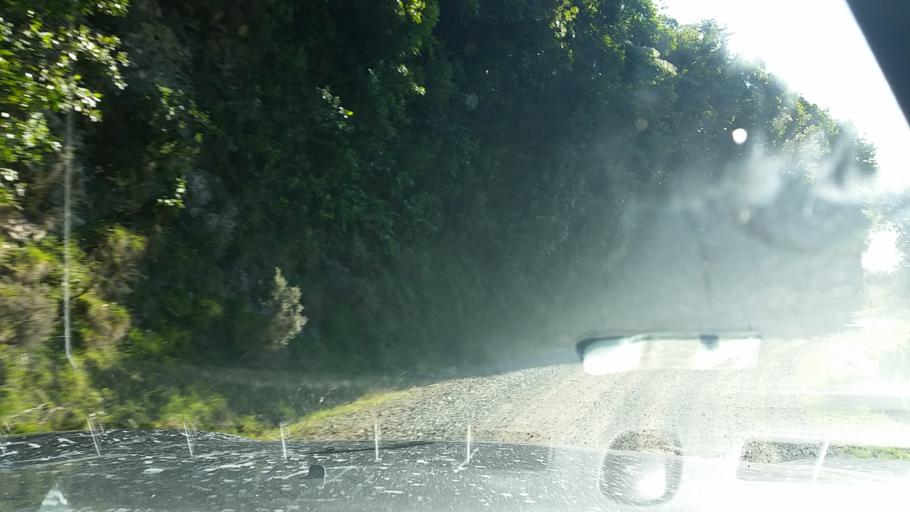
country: NZ
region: Marlborough
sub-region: Marlborough District
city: Picton
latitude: -41.0238
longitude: 174.1569
